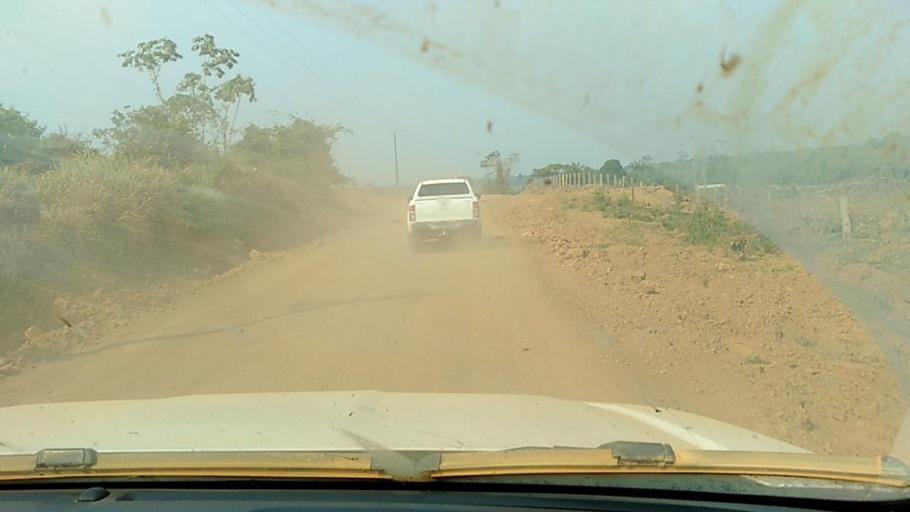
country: BR
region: Rondonia
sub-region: Porto Velho
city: Porto Velho
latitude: -8.8556
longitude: -64.1732
